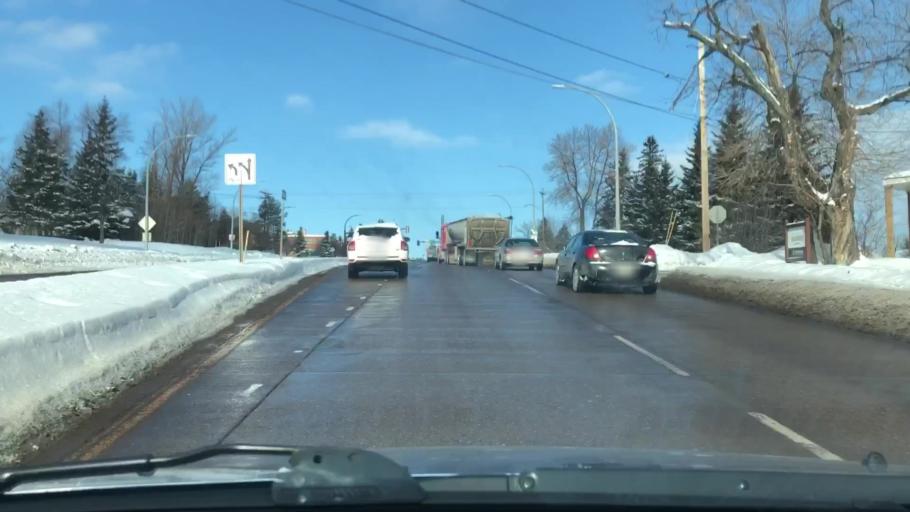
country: US
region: Minnesota
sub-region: Saint Louis County
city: Duluth
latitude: 46.7945
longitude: -92.1070
